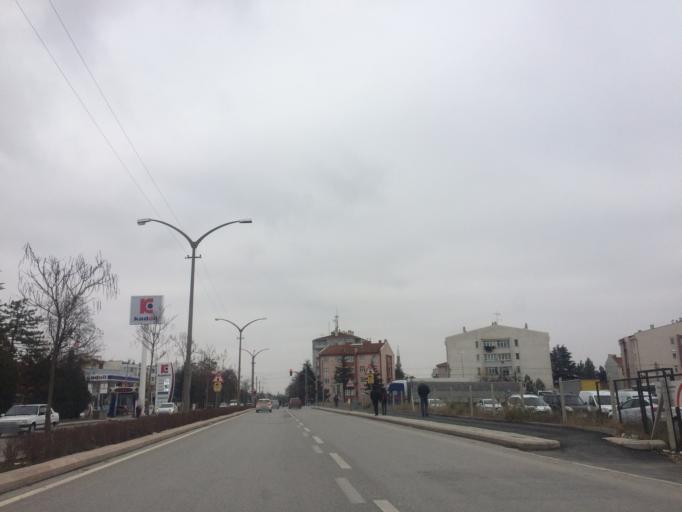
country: TR
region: Eskisehir
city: Eskisehir
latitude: 39.7904
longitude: 30.4807
